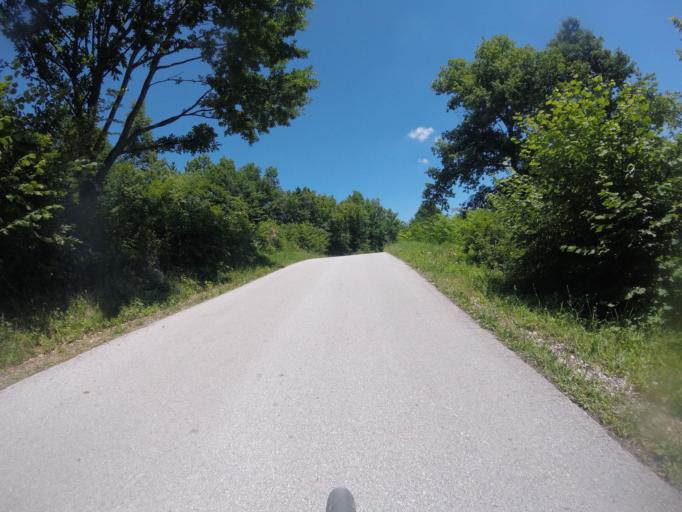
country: SI
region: Metlika
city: Metlika
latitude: 45.7148
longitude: 15.3874
